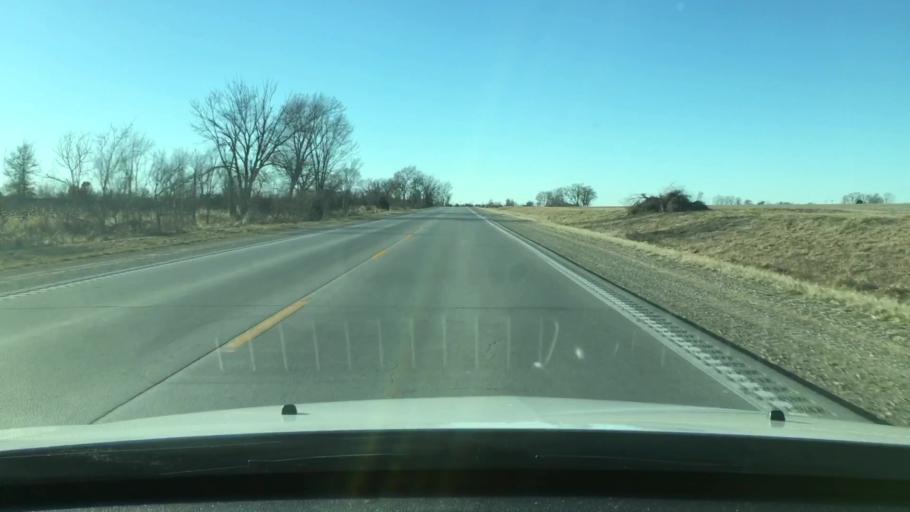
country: US
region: Missouri
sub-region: Audrain County
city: Mexico
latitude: 39.1907
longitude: -92.0021
